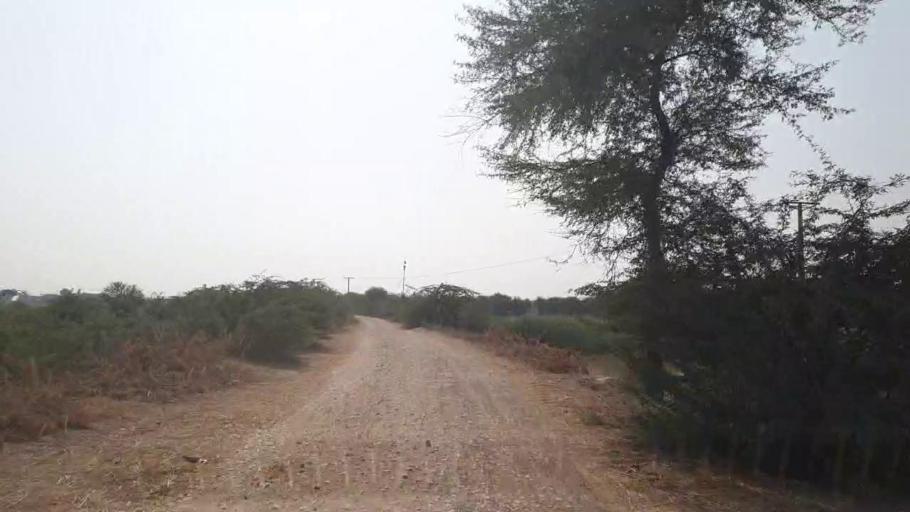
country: PK
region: Sindh
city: Kario
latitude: 24.9059
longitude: 68.5755
